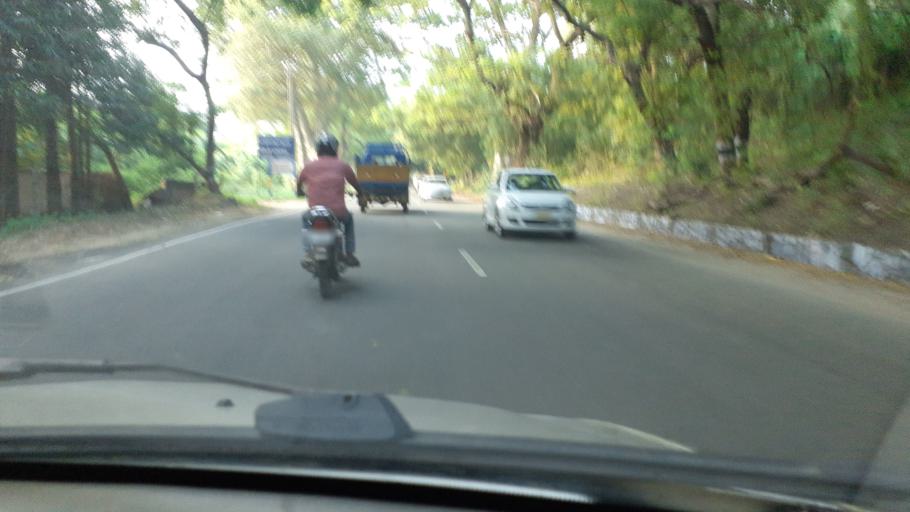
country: IN
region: Tamil Nadu
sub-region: Thoothukkudi
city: Srivaikuntam
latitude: 8.6286
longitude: 77.9065
